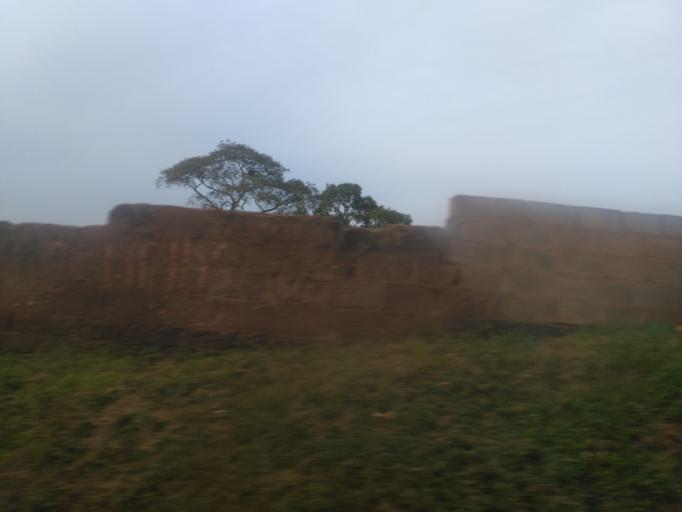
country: UG
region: Central Region
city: Kampala Central Division
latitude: 0.3441
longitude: 32.5730
